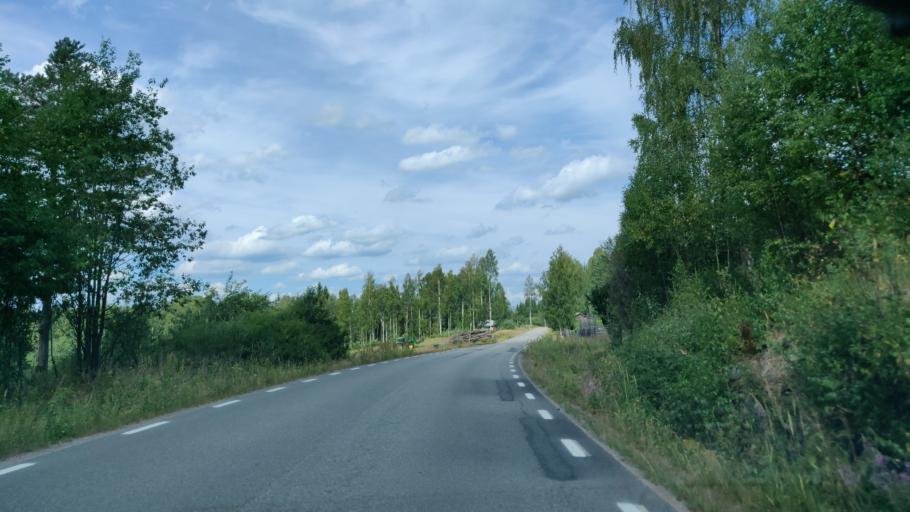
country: SE
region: Vaermland
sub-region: Hagfors Kommun
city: Ekshaerad
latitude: 60.1013
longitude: 13.5005
